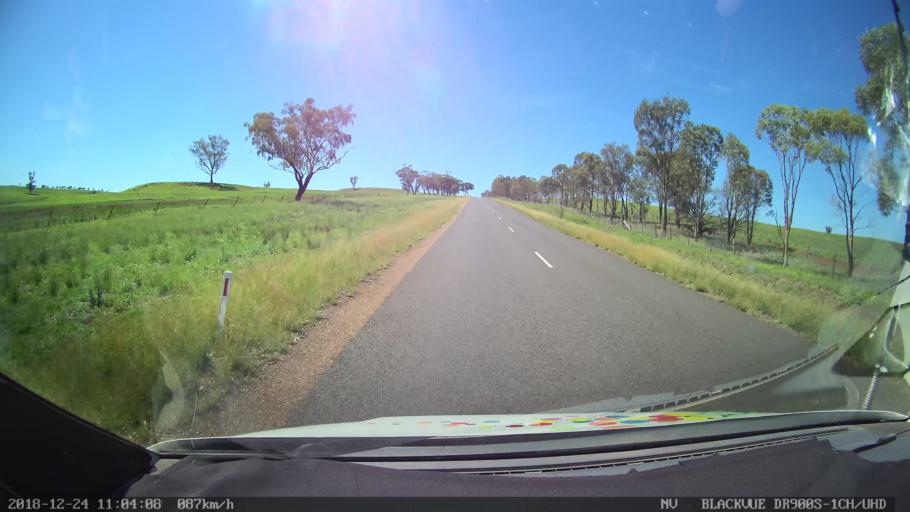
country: AU
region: New South Wales
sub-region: Upper Hunter Shire
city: Merriwa
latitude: -32.1055
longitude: 150.3705
